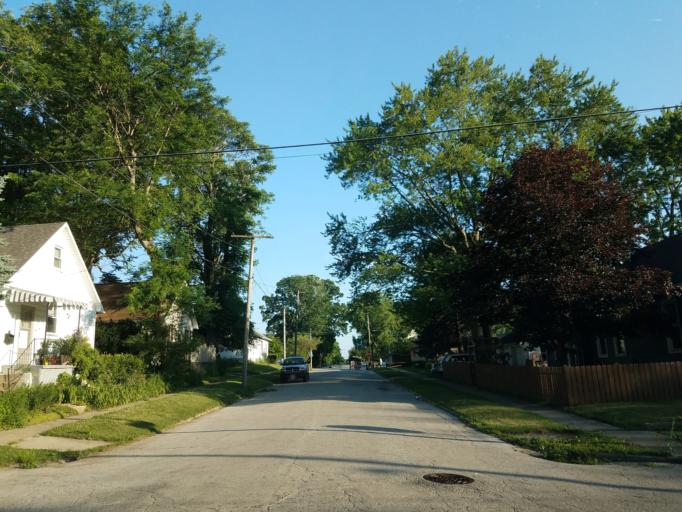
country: US
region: Illinois
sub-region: McLean County
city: Bloomington
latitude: 40.4719
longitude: -89.0099
